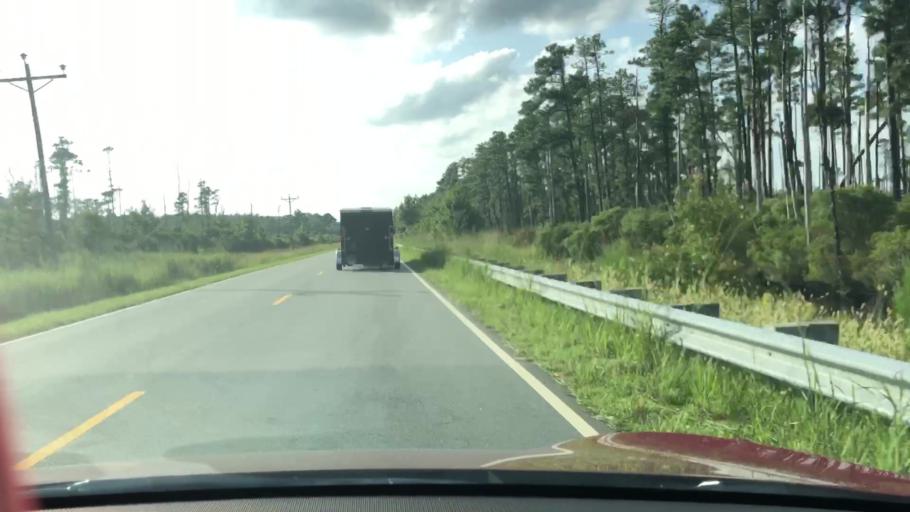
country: US
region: North Carolina
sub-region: Dare County
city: Wanchese
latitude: 35.6108
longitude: -75.8233
